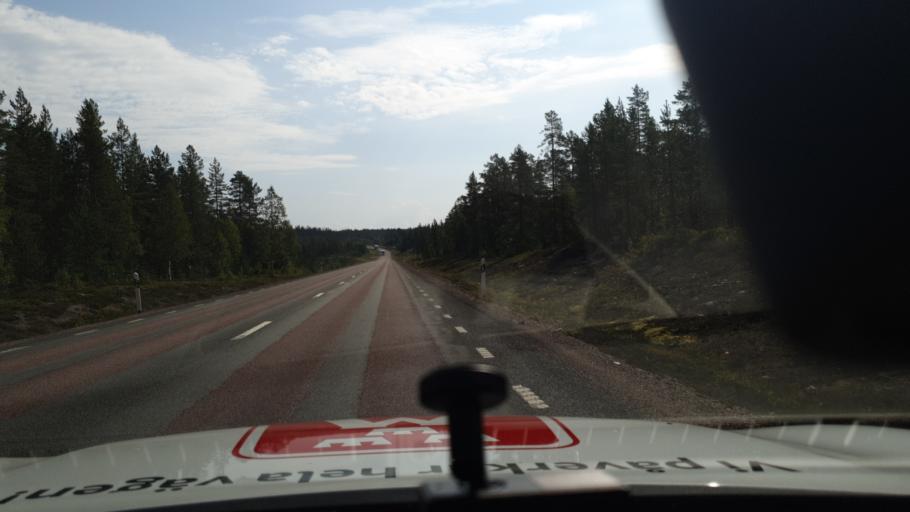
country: SE
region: Dalarna
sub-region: Malung-Saelens kommun
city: Malung
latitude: 60.5155
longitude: 13.4592
